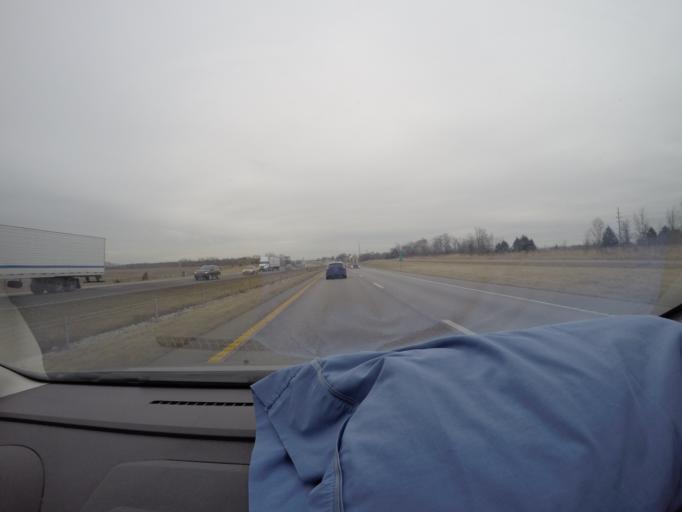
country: US
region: Missouri
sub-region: Warren County
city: Wright City
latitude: 38.8189
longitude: -90.9702
